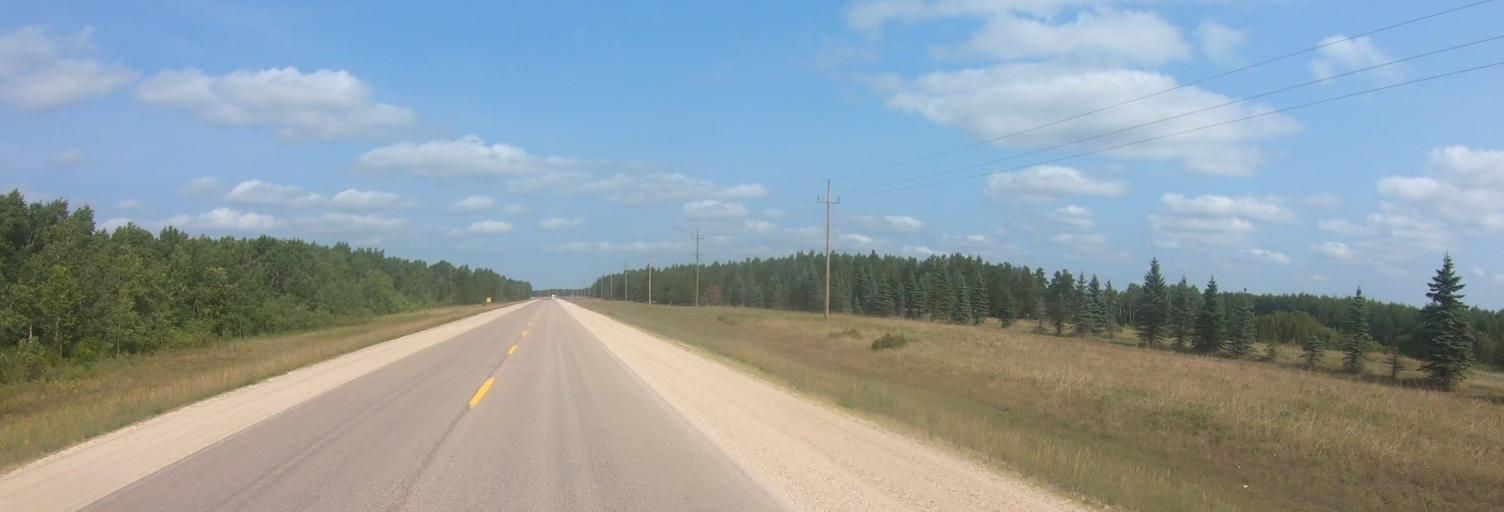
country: CA
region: Manitoba
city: La Broquerie
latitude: 49.2529
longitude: -96.3554
